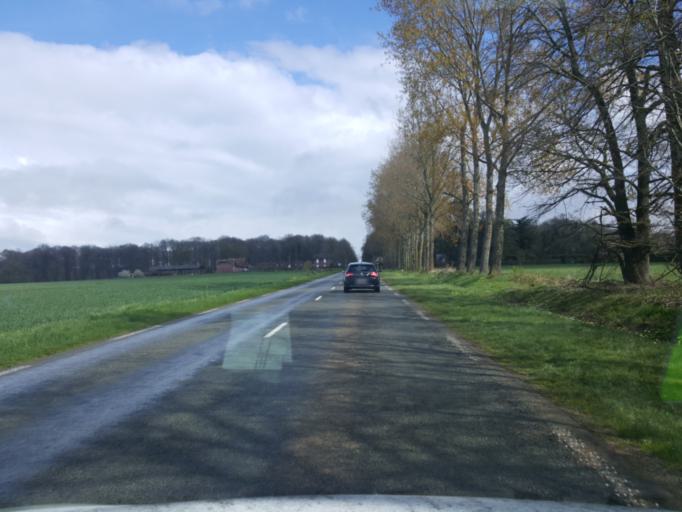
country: FR
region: Picardie
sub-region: Departement de l'Oise
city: Ons-en-Bray
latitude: 49.3433
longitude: 1.9249
